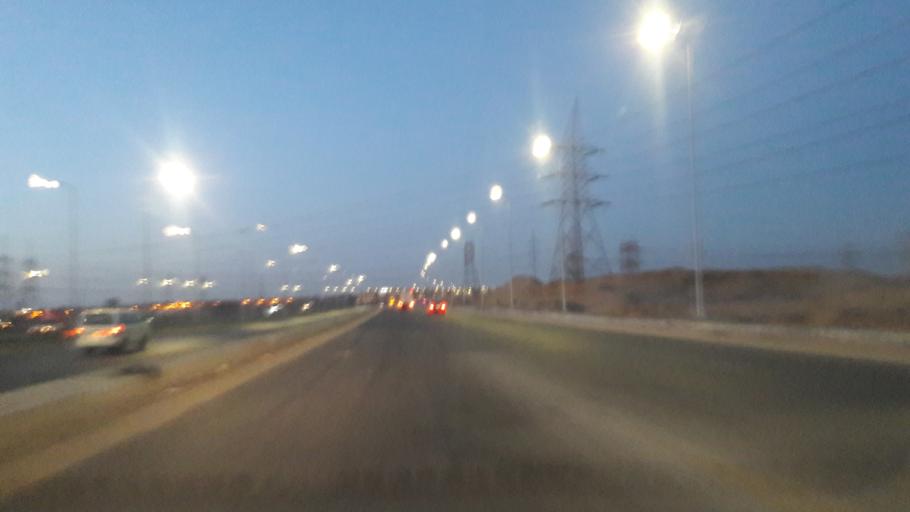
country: EG
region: Al Jizah
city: Madinat Sittah Uktubar
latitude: 29.9433
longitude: 30.9488
